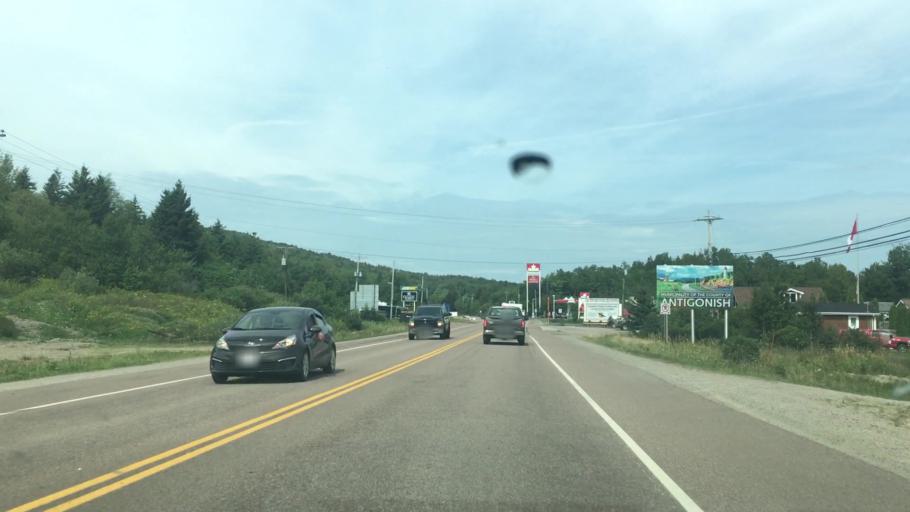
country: CA
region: Nova Scotia
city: Port Hawkesbury
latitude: 45.6512
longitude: -61.4427
